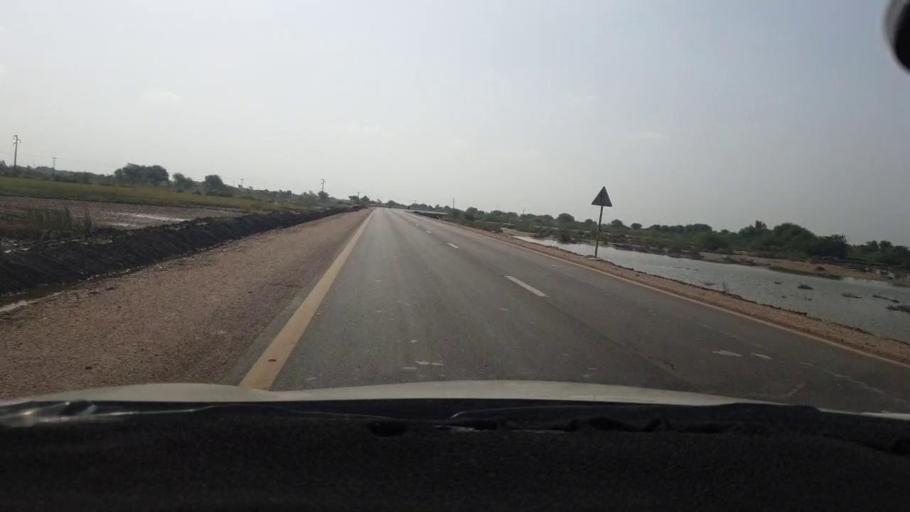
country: PK
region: Sindh
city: Jhol
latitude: 25.8595
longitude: 69.0578
